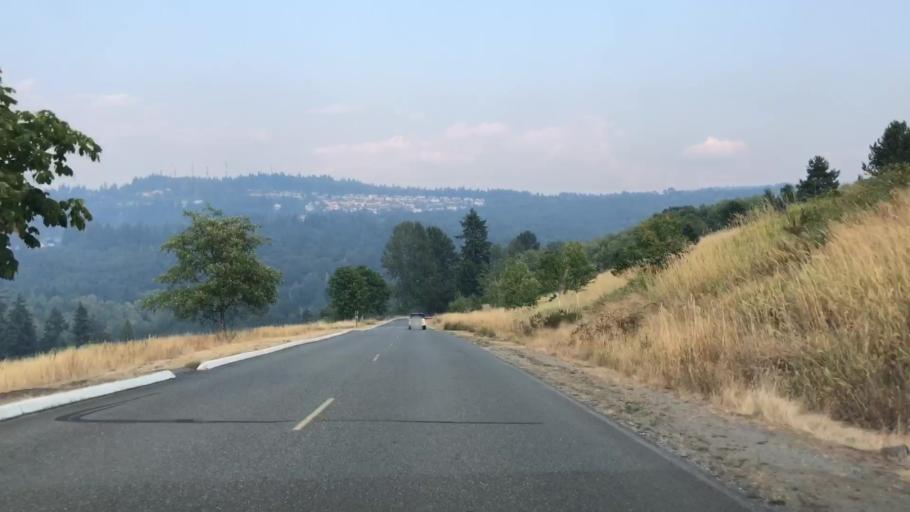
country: US
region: Washington
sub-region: King County
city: Newcastle
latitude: 47.5363
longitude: -122.1403
